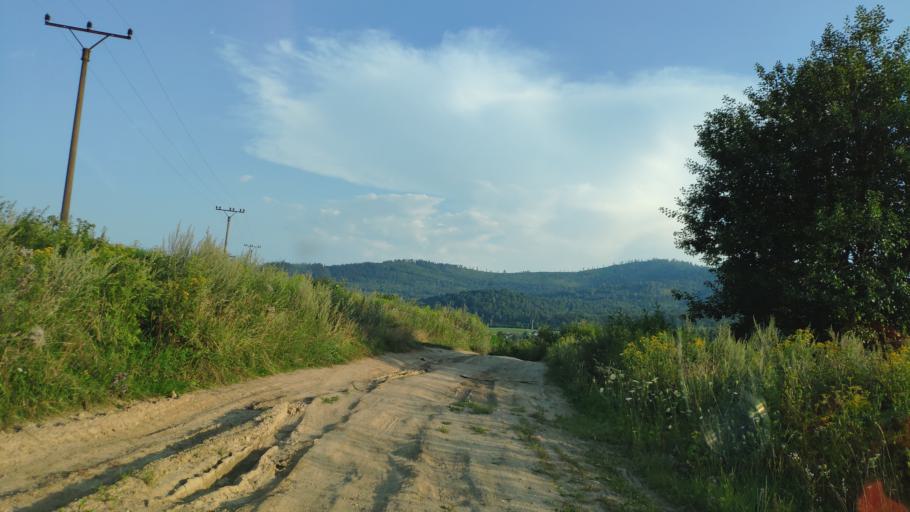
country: SK
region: Kosicky
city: Dobsina
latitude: 48.7177
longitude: 20.2804
